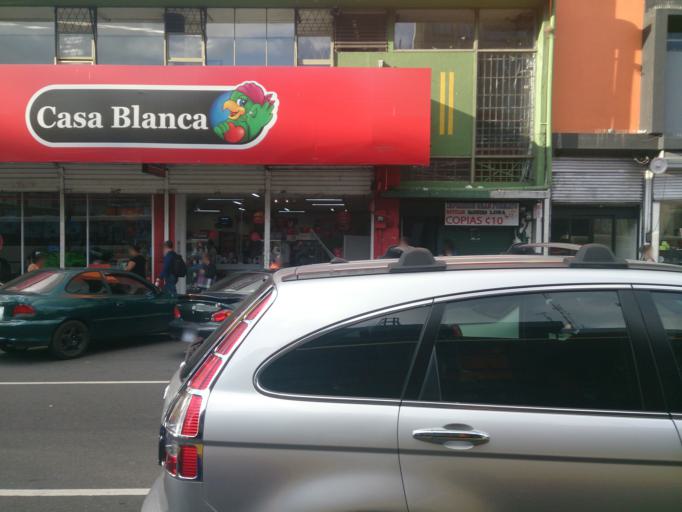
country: CR
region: San Jose
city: San Jose
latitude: 9.9334
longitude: -84.0804
